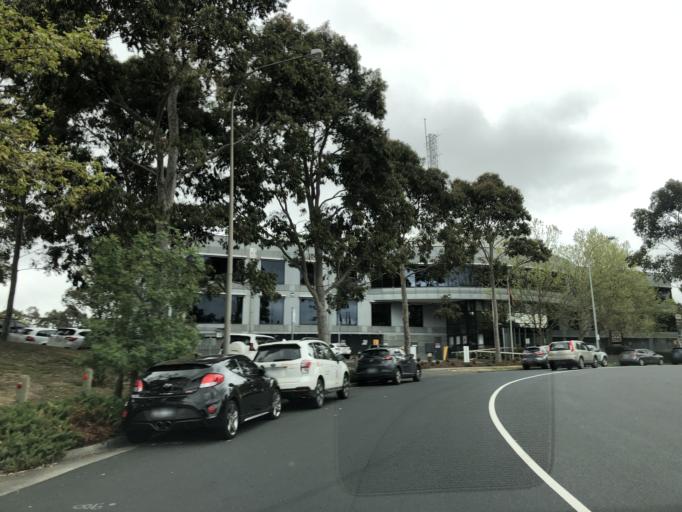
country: AU
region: Victoria
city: Burwood East
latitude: -37.8562
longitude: 145.1647
